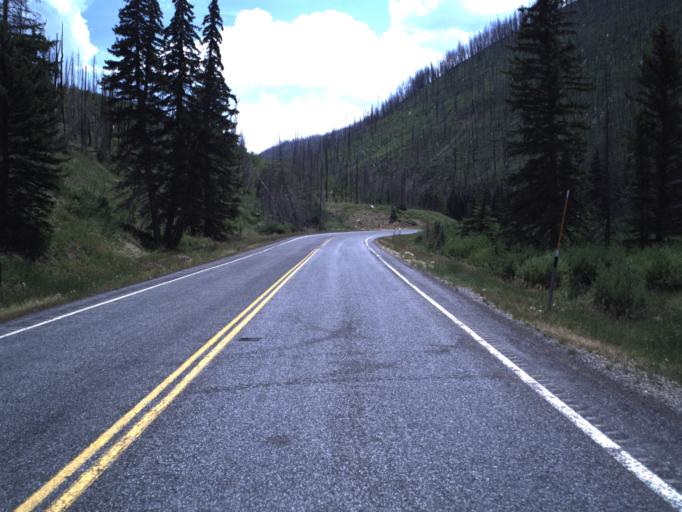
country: US
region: Utah
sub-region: Sanpete County
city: Fairview
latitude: 39.5742
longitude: -111.1829
